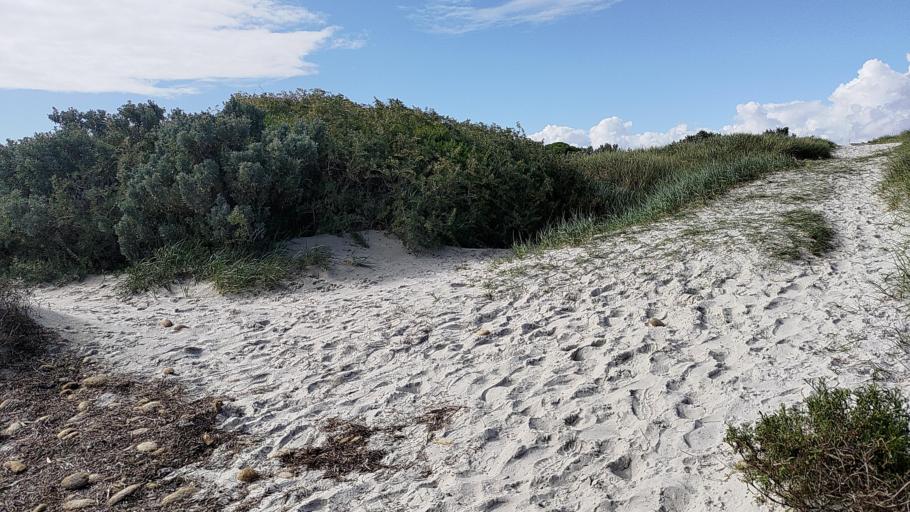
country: AU
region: South Australia
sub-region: Port Adelaide Enfield
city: Birkenhead
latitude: -34.7831
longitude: 138.4784
